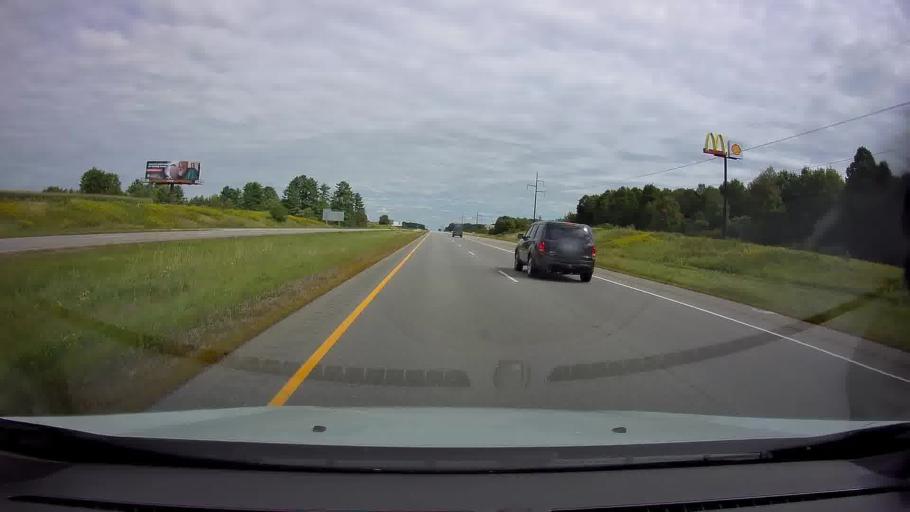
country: US
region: Wisconsin
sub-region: Marathon County
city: Marathon
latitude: 44.9440
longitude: -89.8404
